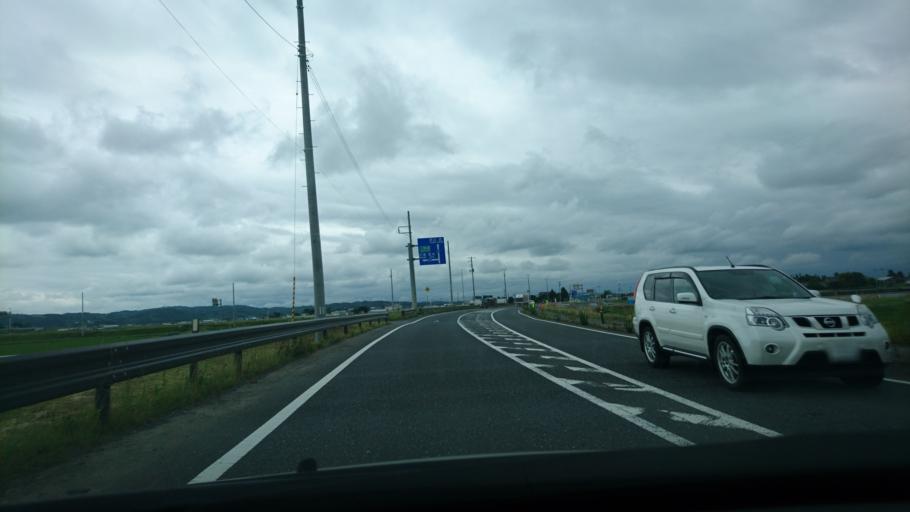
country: JP
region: Miyagi
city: Wakuya
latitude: 38.6790
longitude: 141.2609
